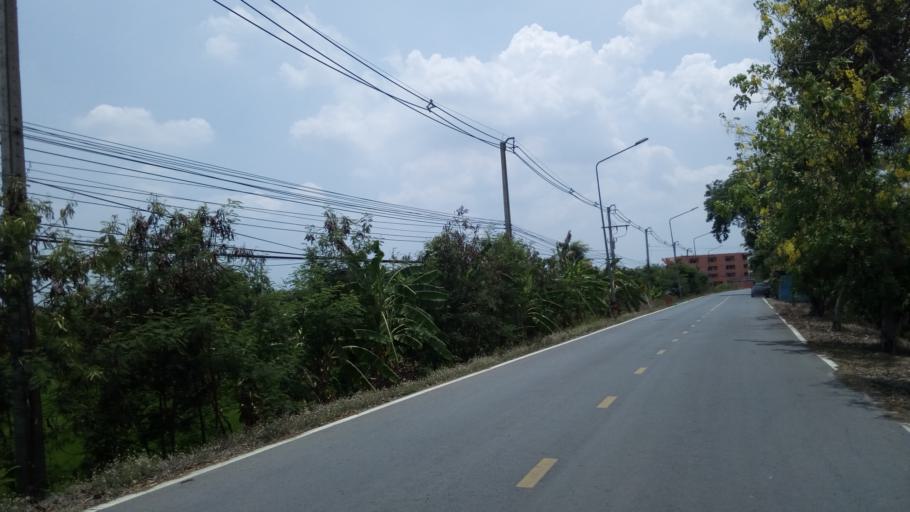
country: TH
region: Pathum Thani
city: Sam Khok
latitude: 14.1022
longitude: 100.5369
